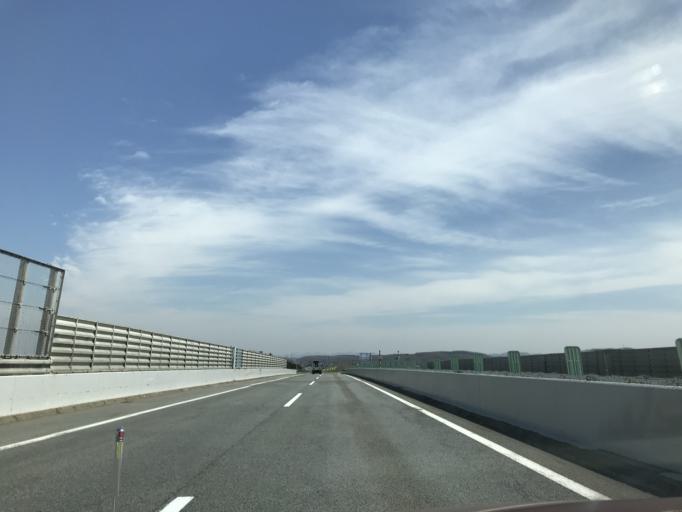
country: JP
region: Hokkaido
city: Iwamizawa
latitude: 43.1633
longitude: 141.7451
